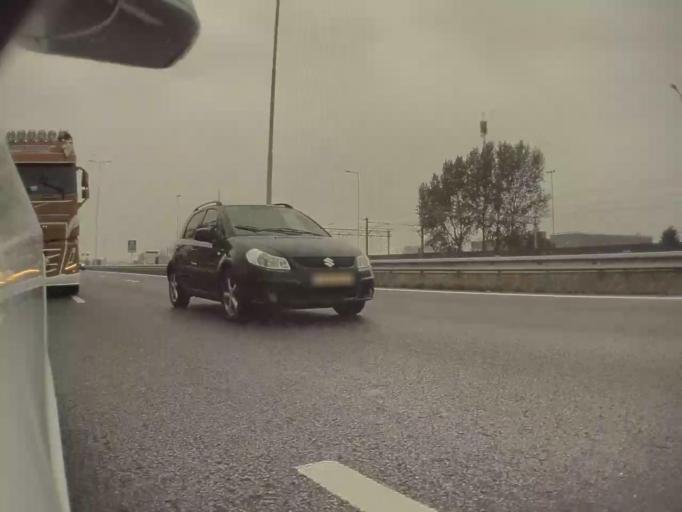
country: NL
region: South Holland
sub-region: Gemeente Spijkenisse
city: Spijkenisse
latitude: 51.8679
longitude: 4.2844
